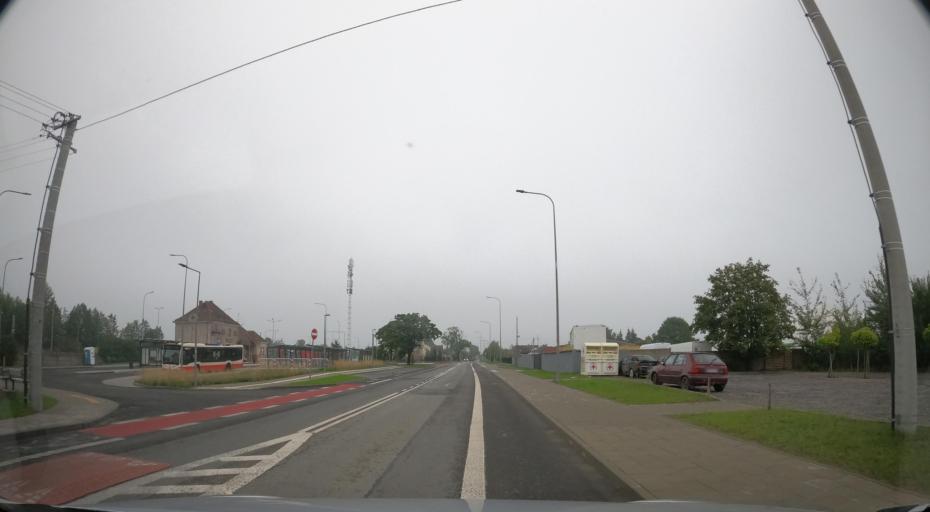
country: PL
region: Pomeranian Voivodeship
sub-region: Powiat kartuski
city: Chwaszczyno
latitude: 54.4202
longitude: 18.4522
